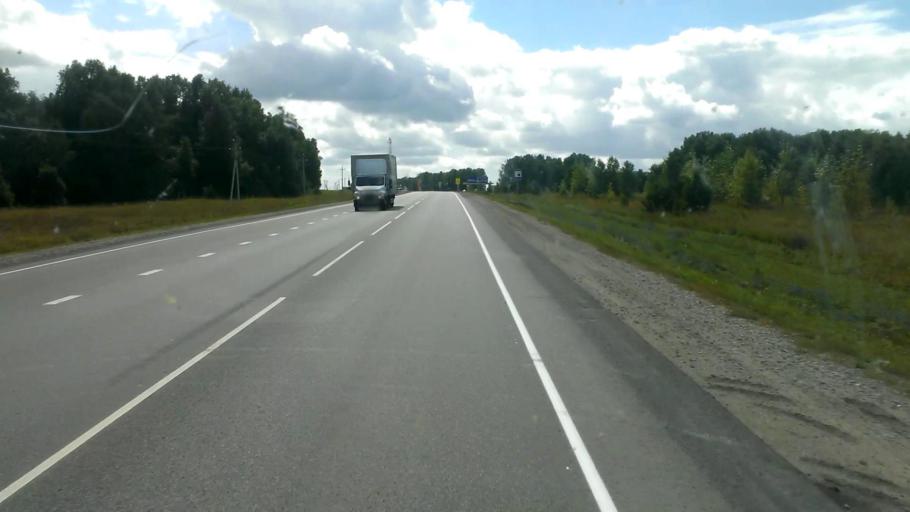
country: RU
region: Altai Krai
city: Troitskoye
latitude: 52.9730
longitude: 84.7477
